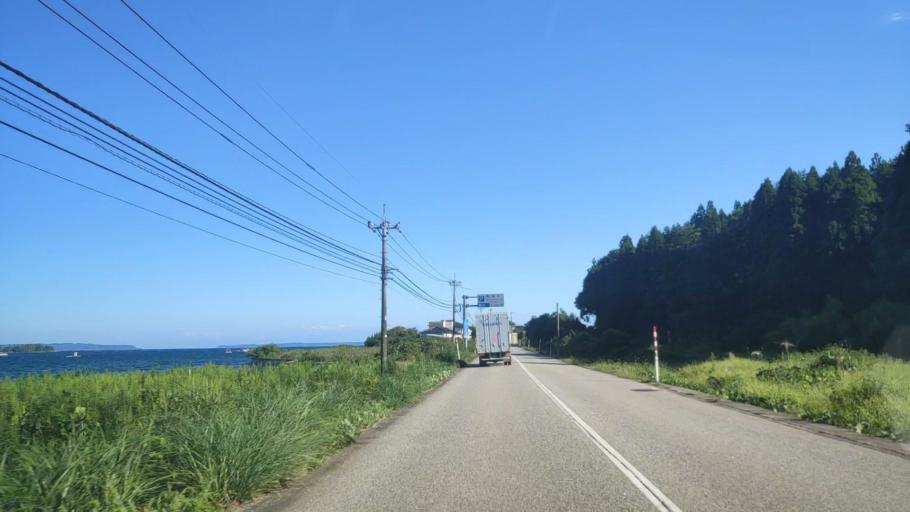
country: JP
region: Ishikawa
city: Nanao
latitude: 37.2003
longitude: 136.9072
